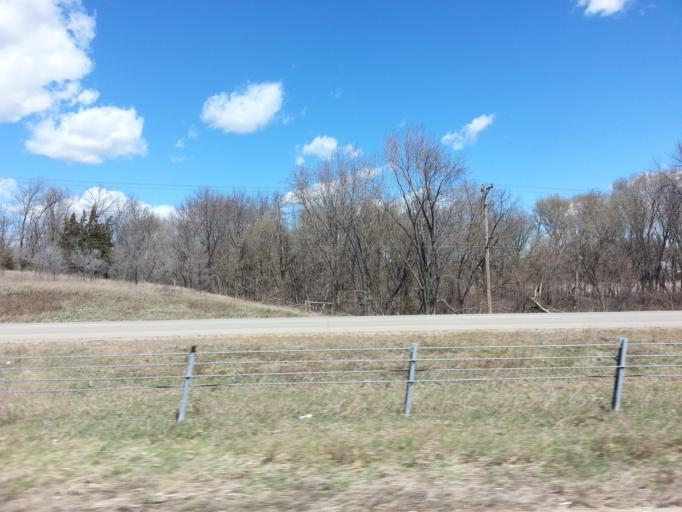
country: US
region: Minnesota
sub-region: Dakota County
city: Hastings
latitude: 44.7840
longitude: -92.8748
